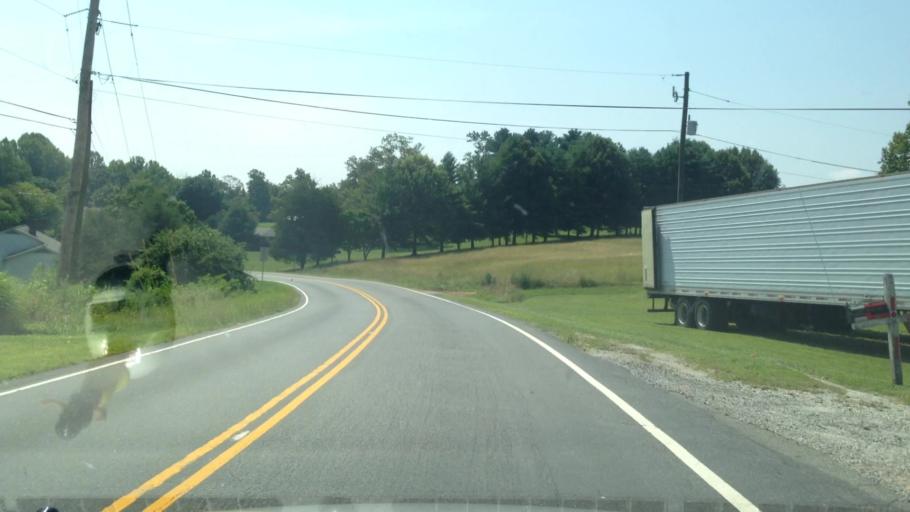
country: US
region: Virginia
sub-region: Patrick County
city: Stuart
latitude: 36.5820
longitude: -80.2777
